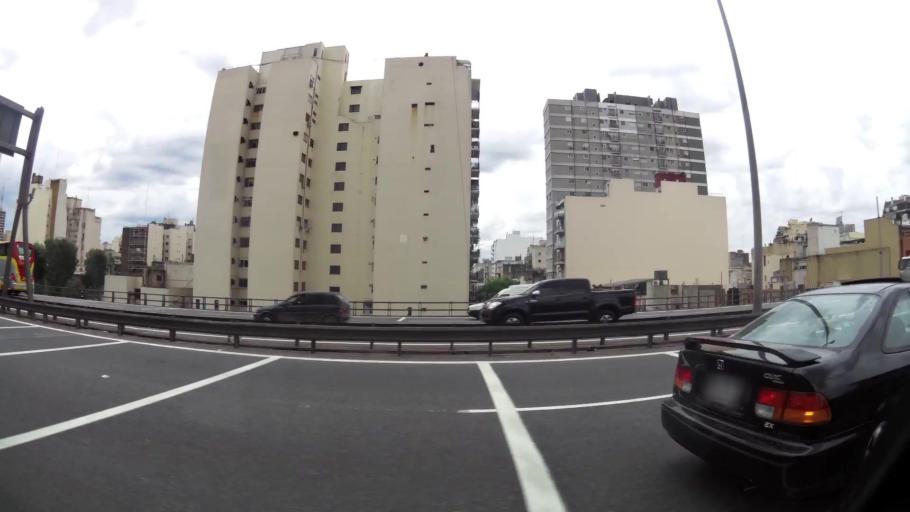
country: AR
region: Buenos Aires F.D.
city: Buenos Aires
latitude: -34.6229
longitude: -58.3742
